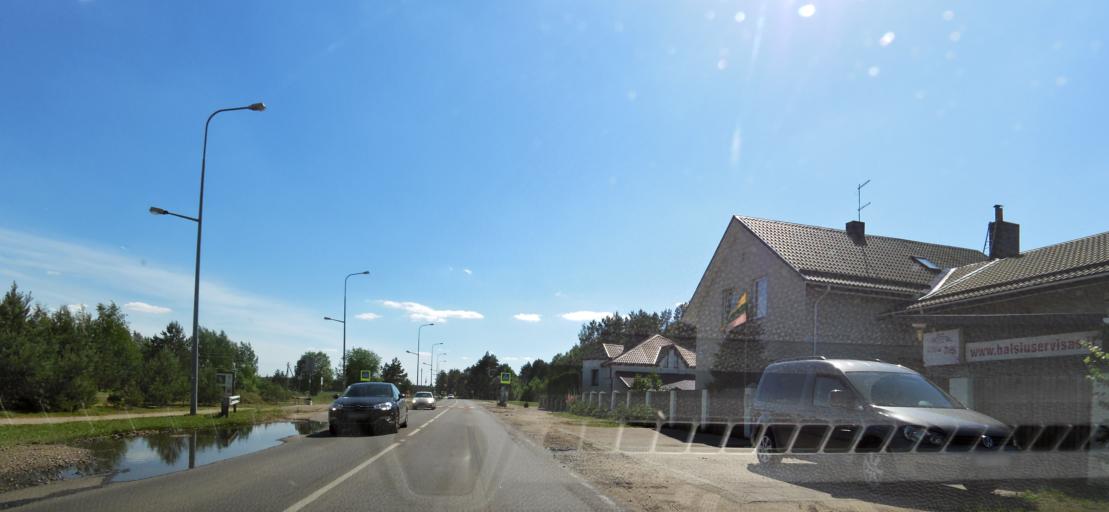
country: LT
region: Vilnius County
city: Rasos
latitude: 54.7812
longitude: 25.3429
